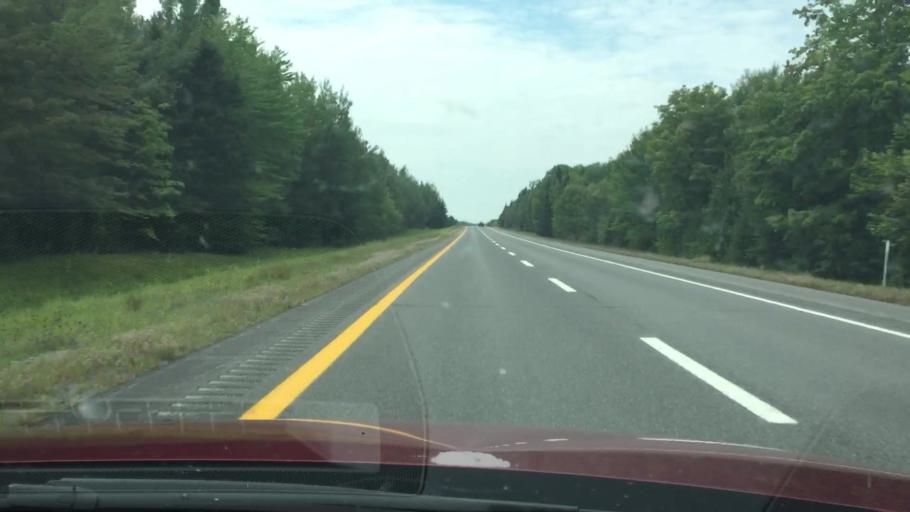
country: US
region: Maine
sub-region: Aroostook County
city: Houlton
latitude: 46.1372
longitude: -67.8842
